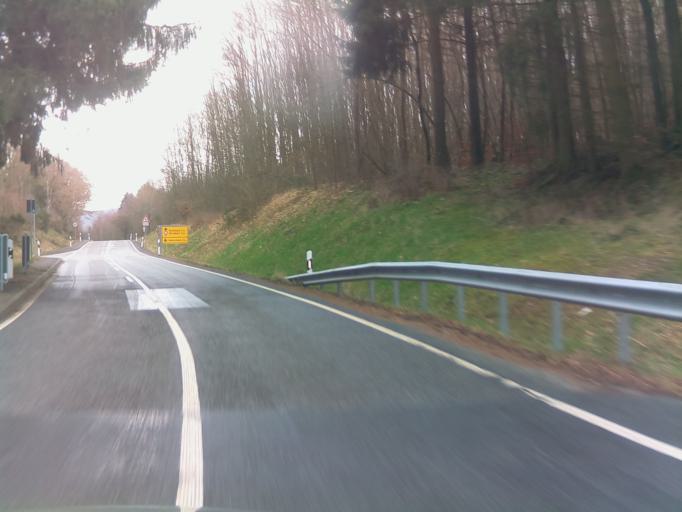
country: DE
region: Rheinland-Pfalz
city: Dorrebach
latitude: 49.9536
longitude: 7.6908
